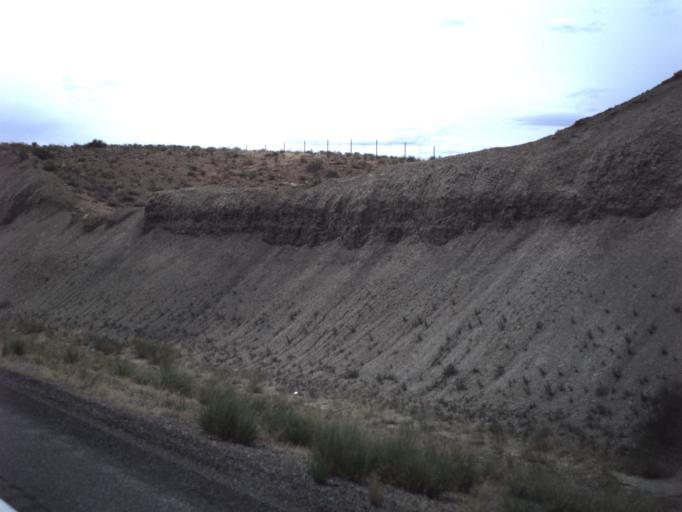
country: US
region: Utah
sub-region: Carbon County
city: East Carbon City
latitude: 39.2776
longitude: -110.3482
